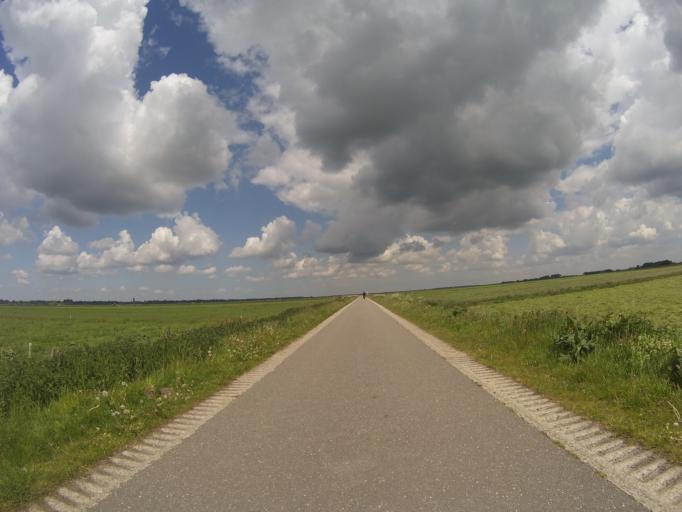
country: NL
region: Utrecht
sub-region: Gemeente Baarn
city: Baarn
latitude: 52.2341
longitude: 5.2851
